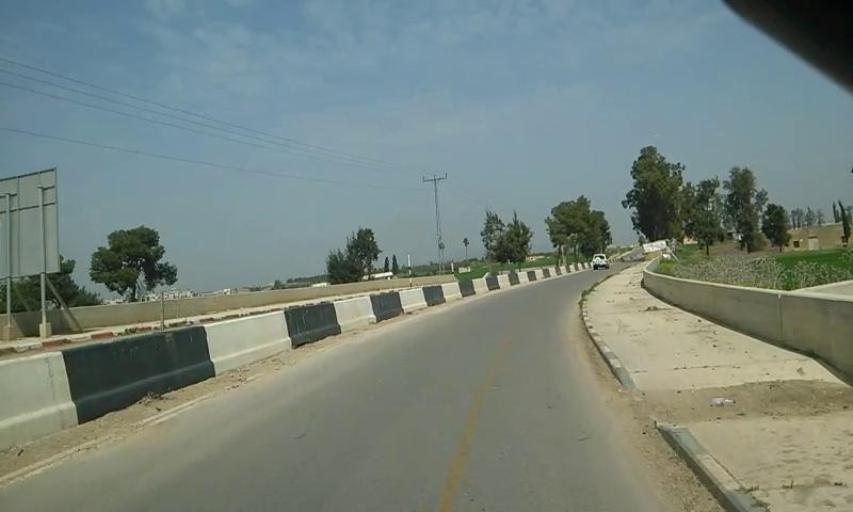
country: PS
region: West Bank
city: Al Jalamah
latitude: 32.5033
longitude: 35.3027
